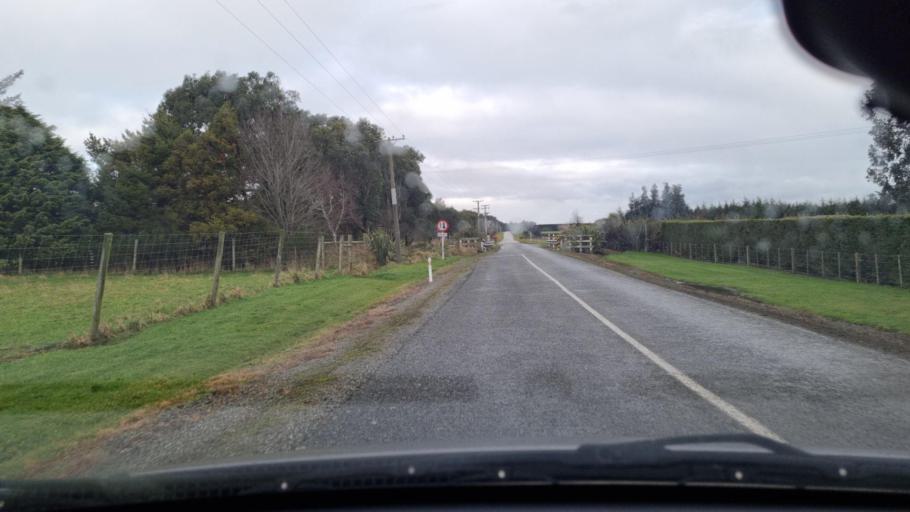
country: NZ
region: Southland
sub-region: Invercargill City
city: Invercargill
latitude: -46.4098
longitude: 168.4396
